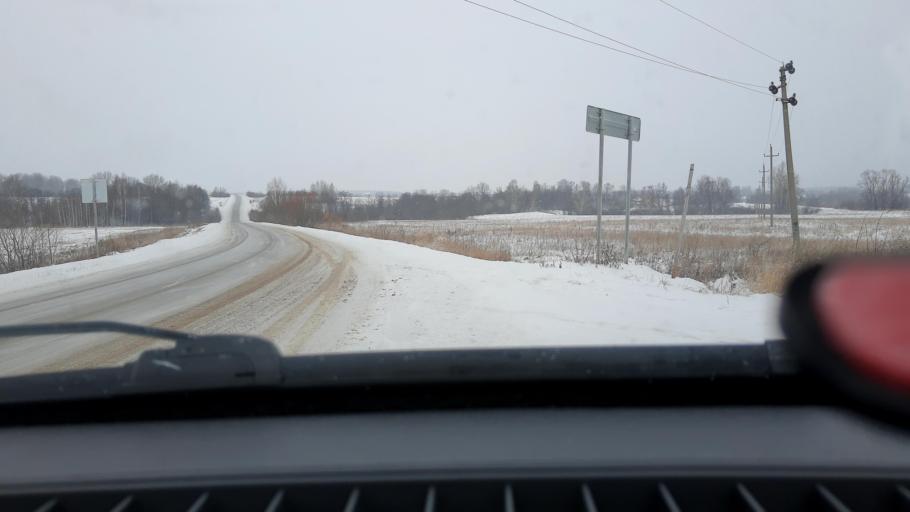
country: RU
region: Bashkortostan
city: Iglino
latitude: 54.6987
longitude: 56.4173
